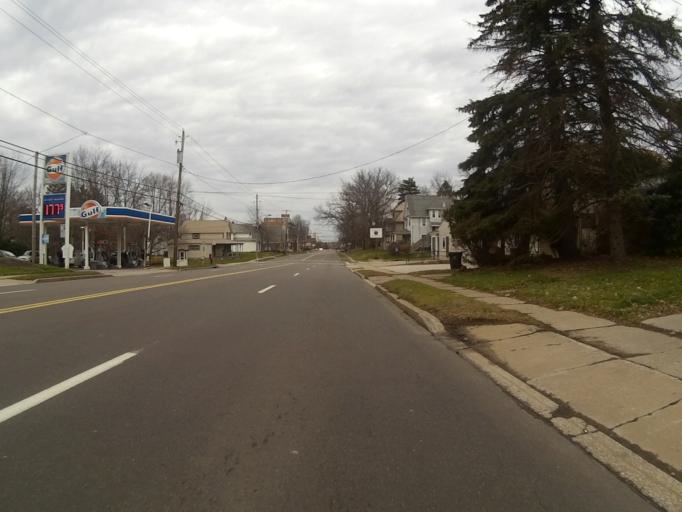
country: US
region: Ohio
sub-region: Portage County
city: Kent
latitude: 41.1463
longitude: -81.3582
